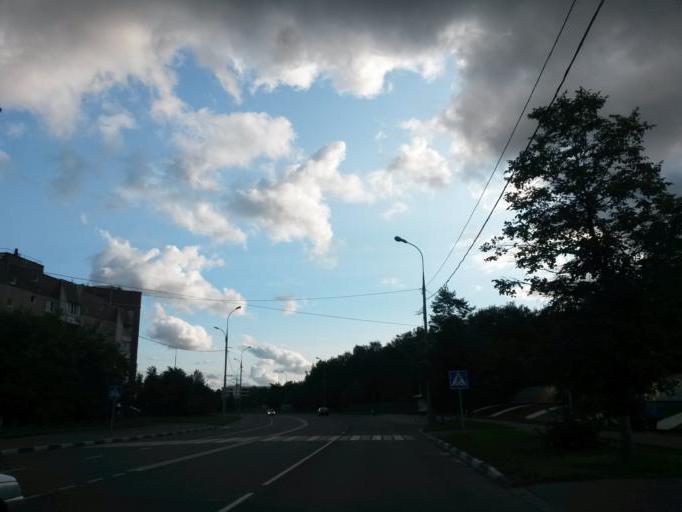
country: RU
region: Moscow
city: Zhulebino
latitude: 55.6874
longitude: 37.8445
